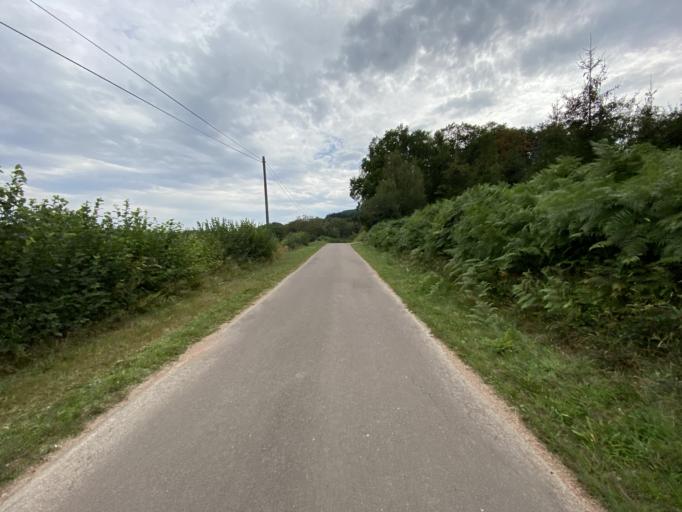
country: FR
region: Bourgogne
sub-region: Departement de la Cote-d'Or
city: Saulieu
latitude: 47.2686
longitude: 4.1353
